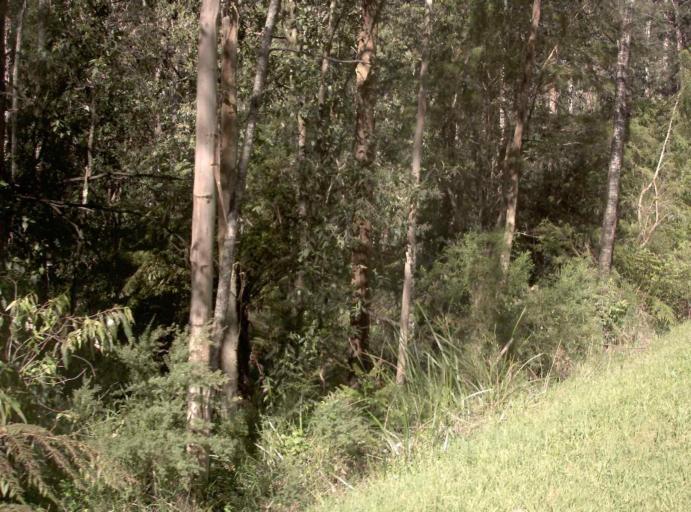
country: AU
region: Victoria
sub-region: Baw Baw
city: Warragul
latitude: -37.8898
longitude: 145.9017
